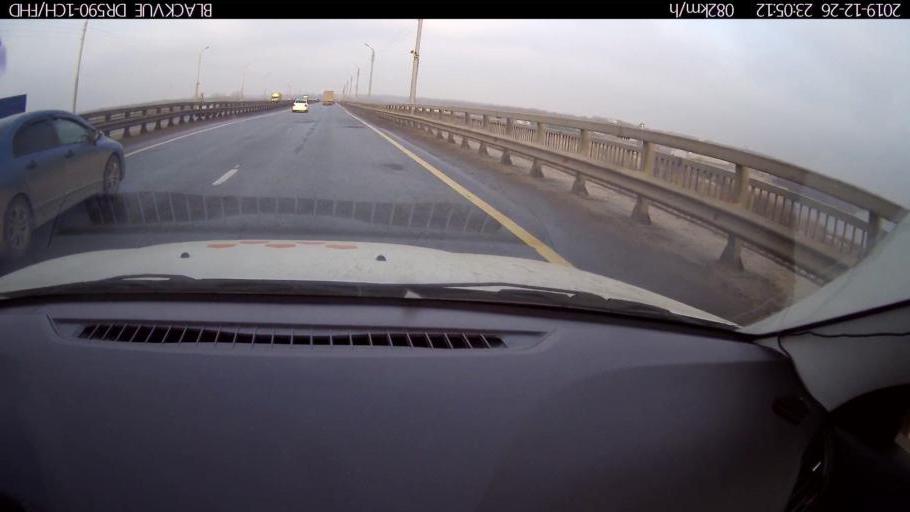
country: RU
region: Nizjnij Novgorod
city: Burevestnik
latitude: 56.1897
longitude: 43.7507
